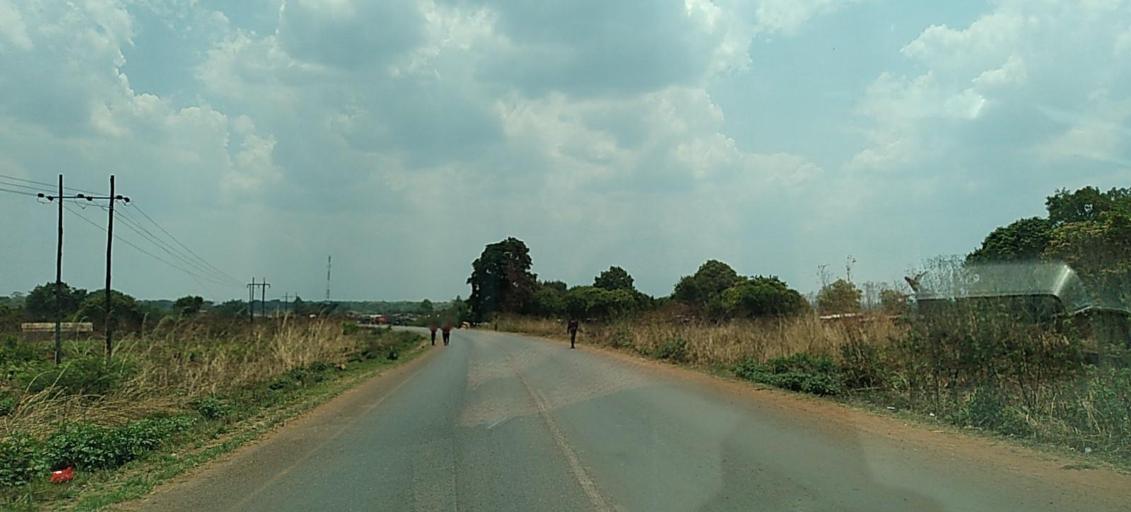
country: ZM
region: Copperbelt
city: Kalulushi
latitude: -12.8344
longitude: 27.9722
